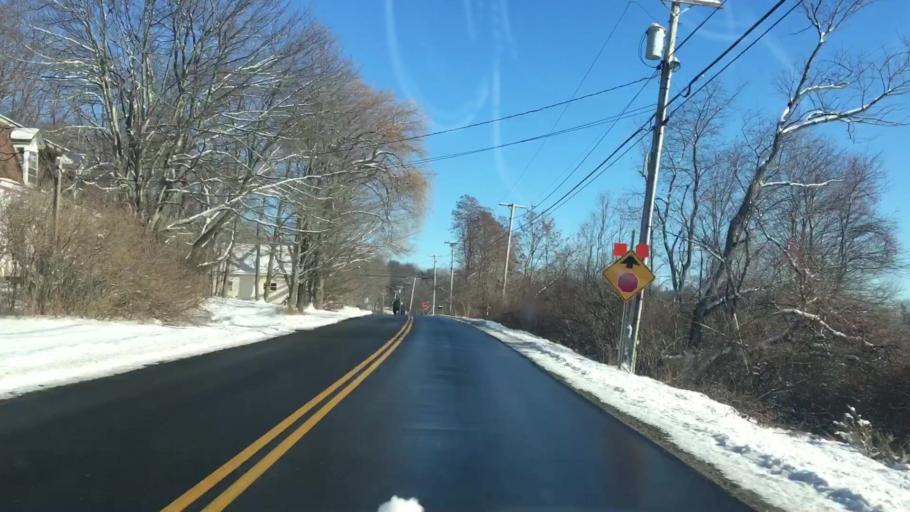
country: US
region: Maine
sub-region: Androscoggin County
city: Lisbon
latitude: 43.9491
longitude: -70.1490
